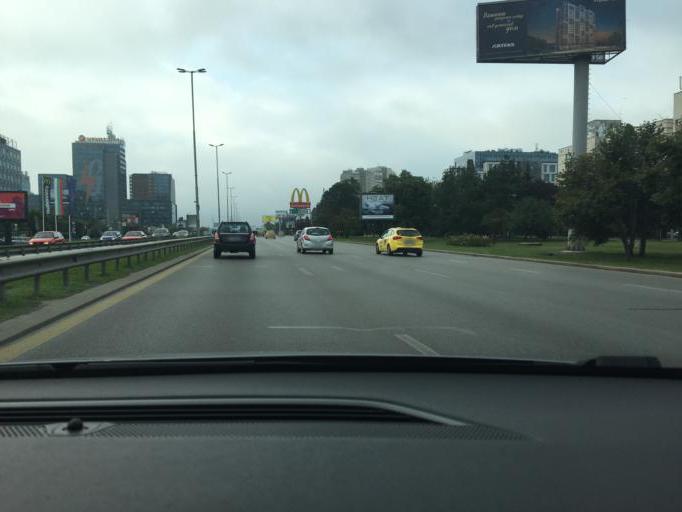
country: BG
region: Sofia-Capital
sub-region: Stolichna Obshtina
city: Sofia
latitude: 42.6619
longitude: 23.3778
